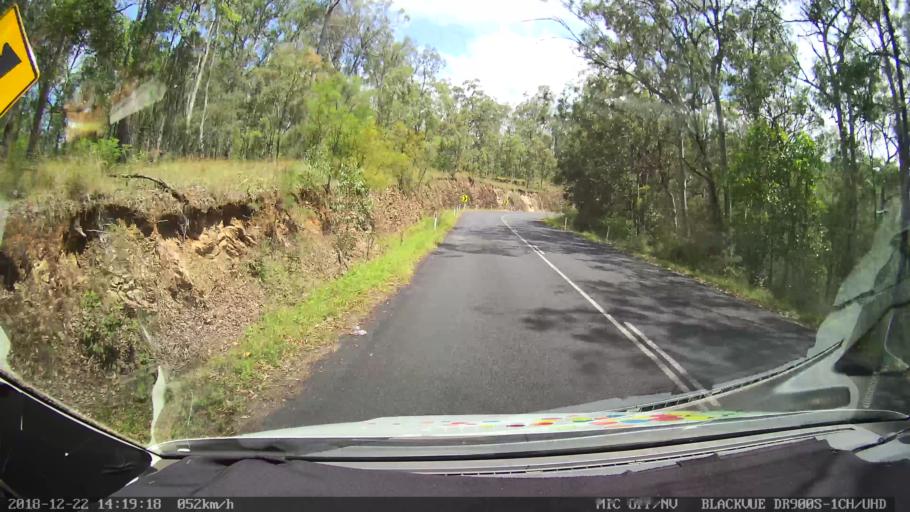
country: AU
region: New South Wales
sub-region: Clarence Valley
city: Coutts Crossing
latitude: -30.0092
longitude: 152.6632
